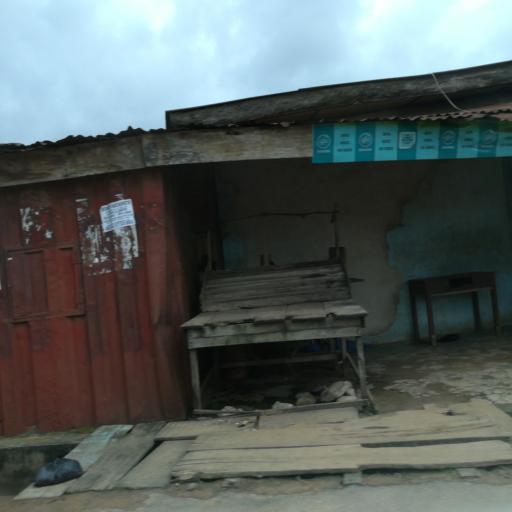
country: NG
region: Lagos
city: Agege
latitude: 6.6075
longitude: 3.2950
